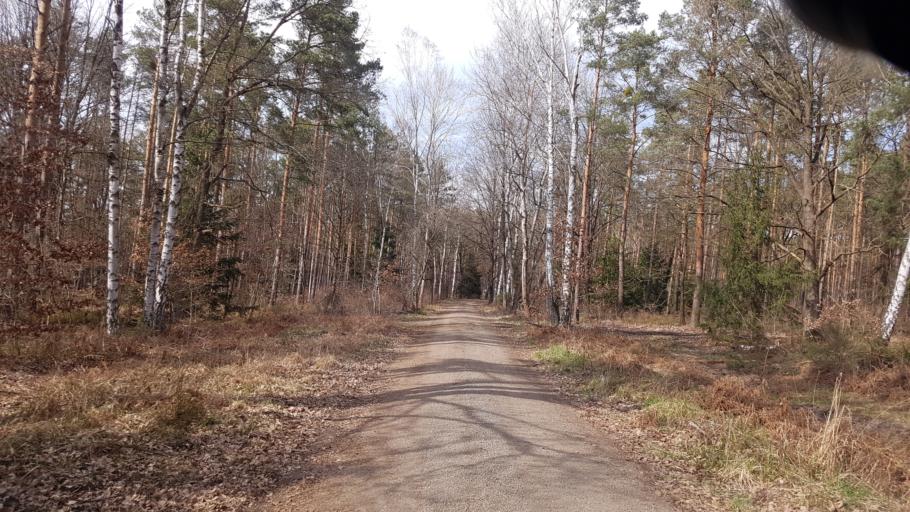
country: DE
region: Brandenburg
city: Lauchhammer
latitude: 51.5353
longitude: 13.7064
